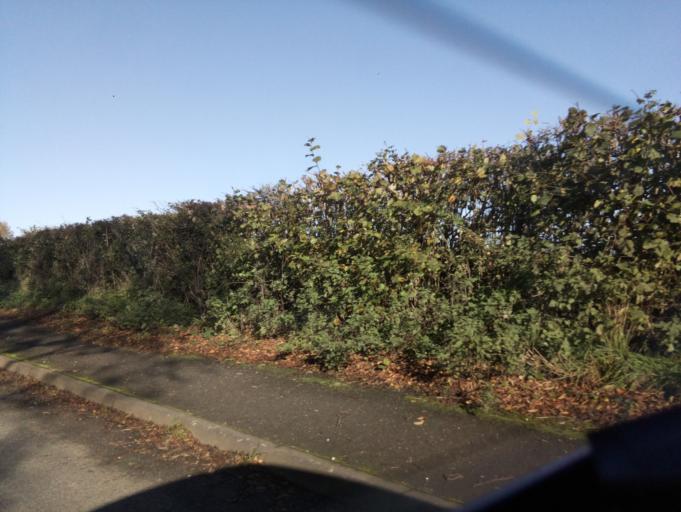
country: GB
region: England
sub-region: Somerset
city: Yeovil
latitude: 50.9594
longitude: -2.6581
